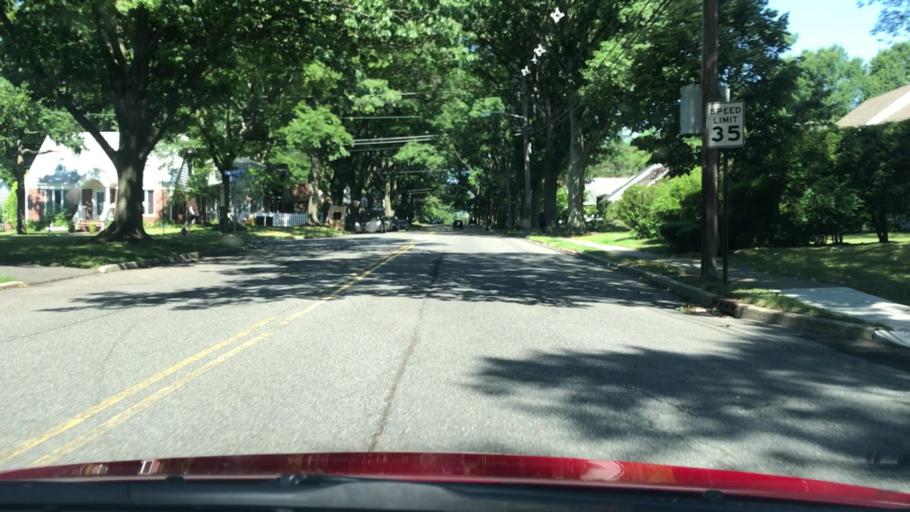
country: US
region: New Jersey
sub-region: Bergen County
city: Teaneck
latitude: 40.8822
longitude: -74.0008
